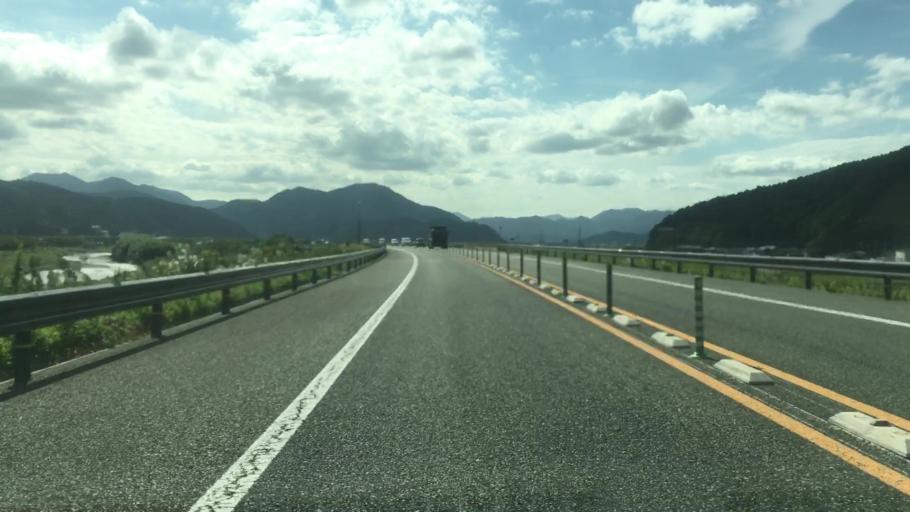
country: JP
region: Kyoto
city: Fukuchiyama
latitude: 35.2107
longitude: 135.0368
